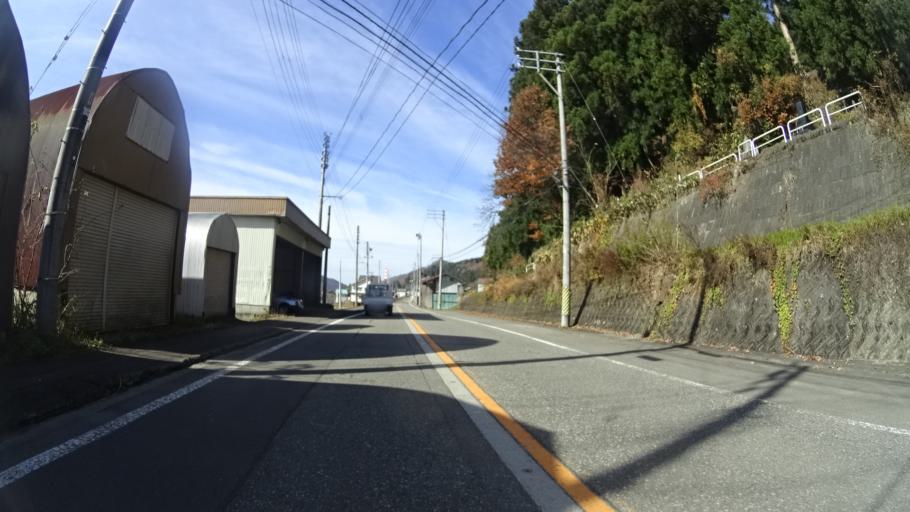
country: JP
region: Niigata
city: Muikamachi
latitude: 37.2084
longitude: 139.0613
